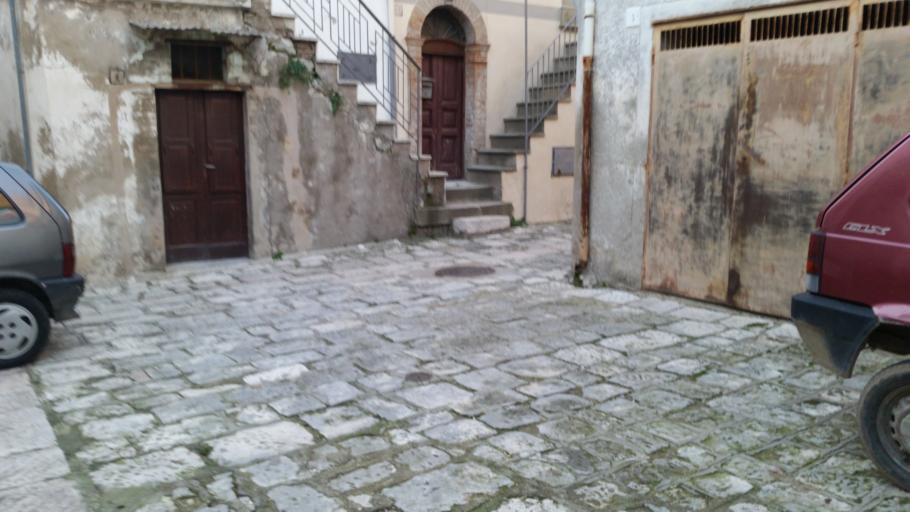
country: IT
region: Basilicate
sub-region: Provincia di Matera
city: Tricarico
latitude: 40.6234
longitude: 16.1437
